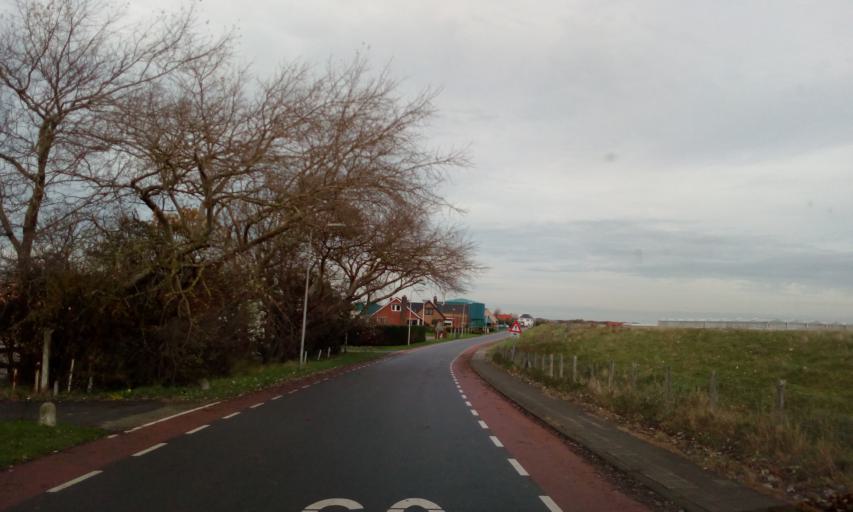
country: NL
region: South Holland
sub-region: Gemeente Westland
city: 's-Gravenzande
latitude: 52.0037
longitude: 4.1517
